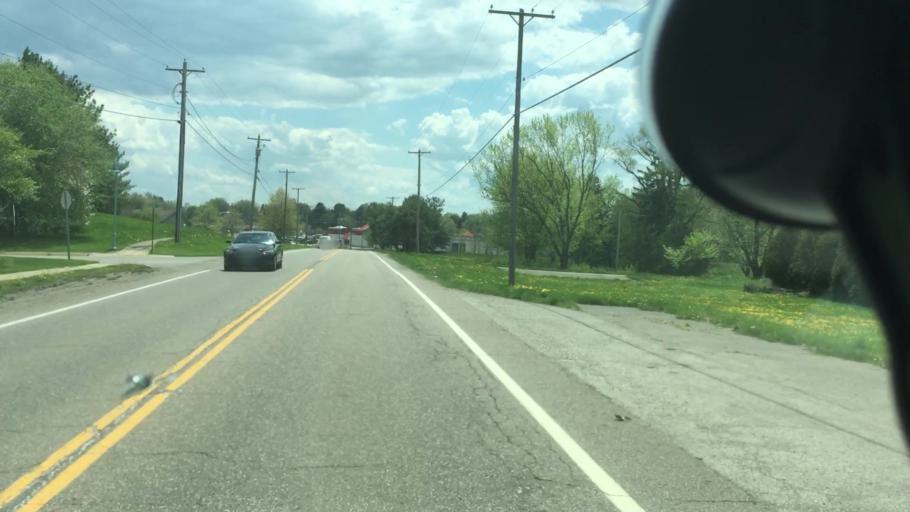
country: US
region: Ohio
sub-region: Columbiana County
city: Columbiana
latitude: 40.9055
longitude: -80.6958
